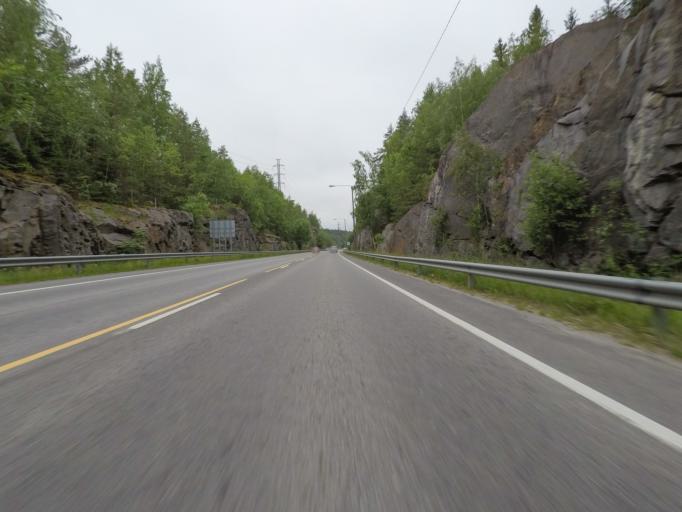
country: FI
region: Varsinais-Suomi
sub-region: Turku
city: Raisio
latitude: 60.4629
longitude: 22.1433
